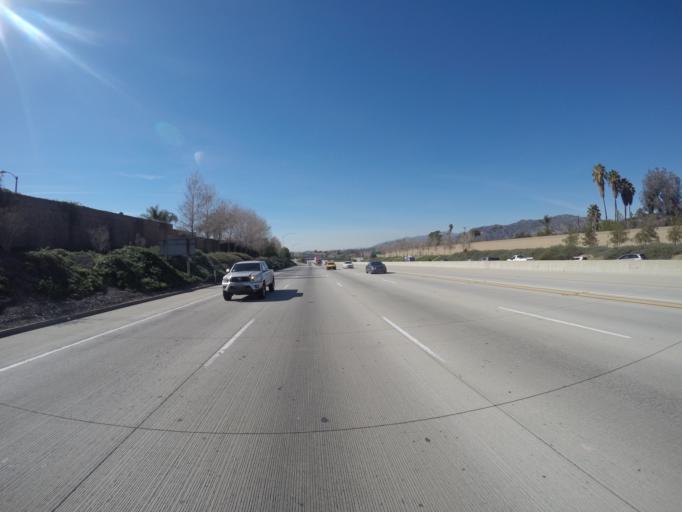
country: US
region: California
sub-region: Los Angeles County
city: La Verne
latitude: 34.1193
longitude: -117.7530
